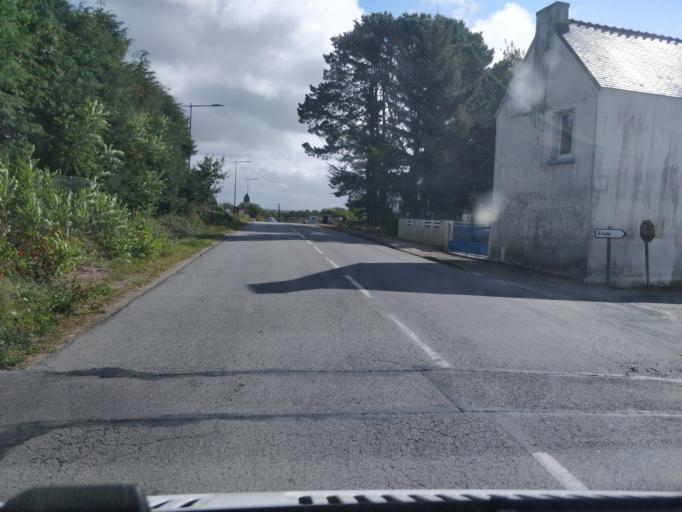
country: FR
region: Brittany
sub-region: Departement du Finistere
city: Landudec
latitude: 48.0001
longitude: -4.3291
